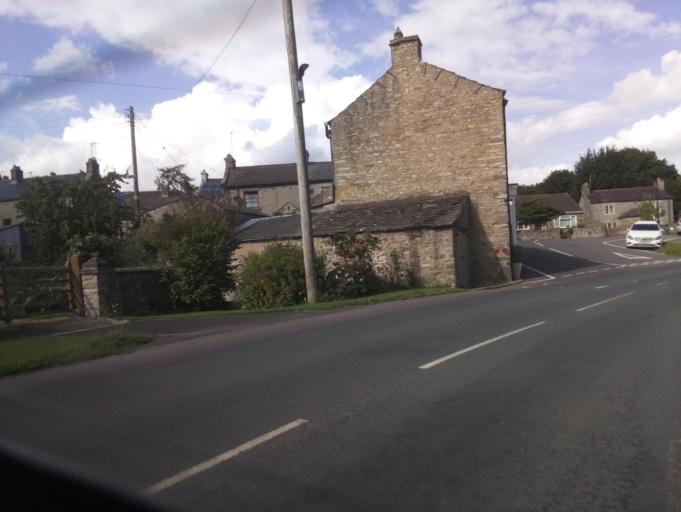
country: GB
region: England
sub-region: North Yorkshire
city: Leyburn
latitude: 54.3311
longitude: -1.8251
